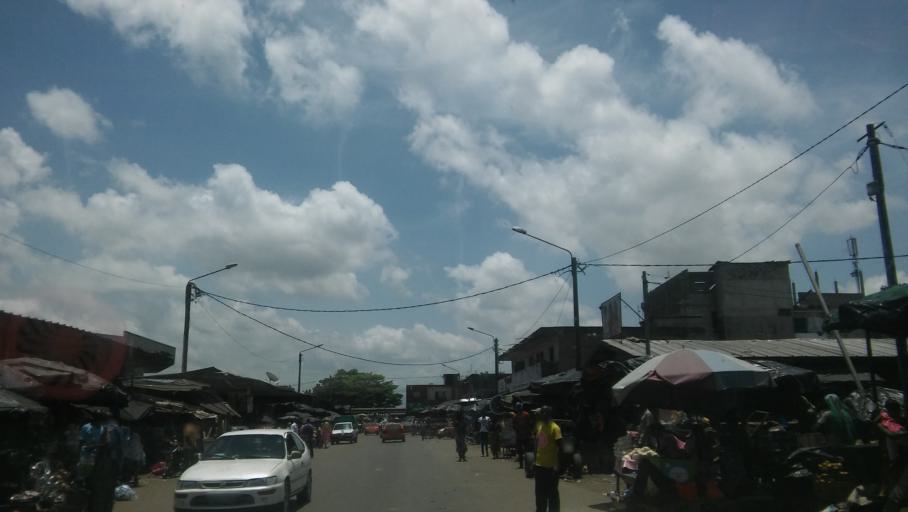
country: CI
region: Lagunes
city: Abidjan
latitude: 5.2909
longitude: -3.9586
